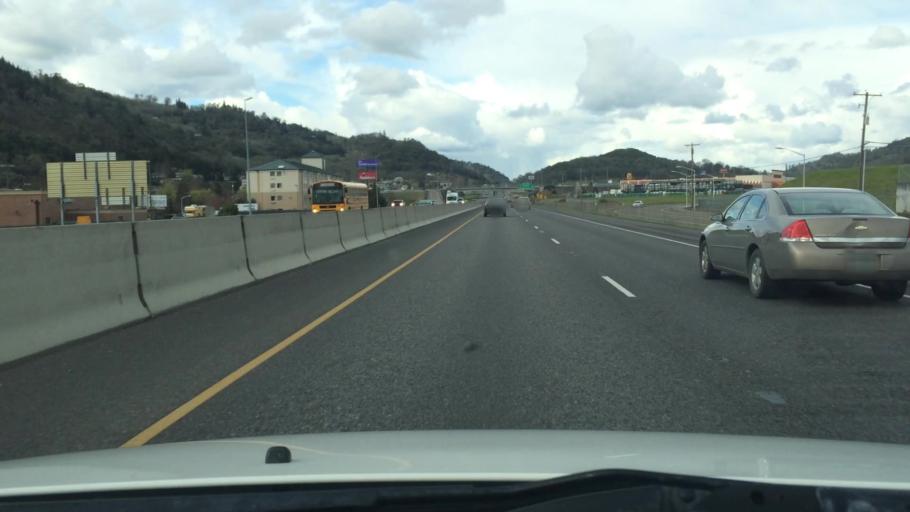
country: US
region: Oregon
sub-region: Douglas County
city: Roseburg
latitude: 43.2414
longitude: -123.3603
